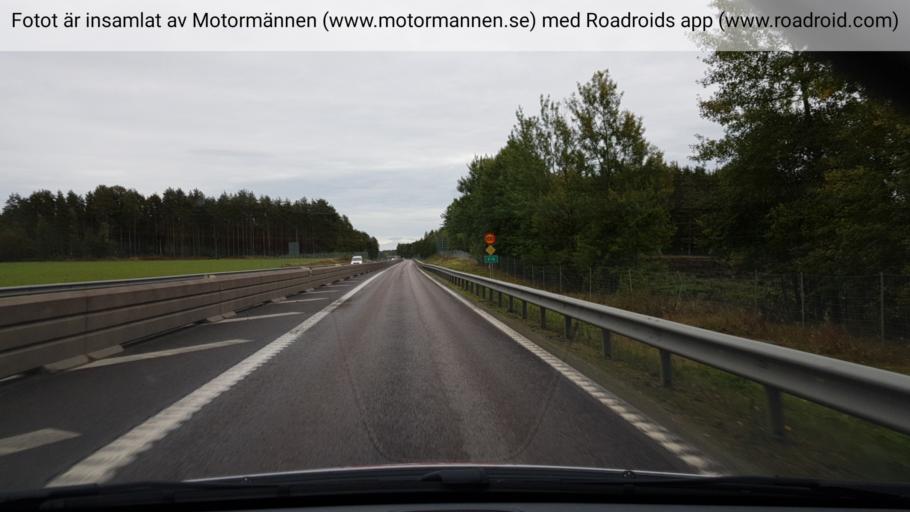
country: SE
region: Vaermland
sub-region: Karlstads Kommun
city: Edsvalla
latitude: 59.3872
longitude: 13.2374
